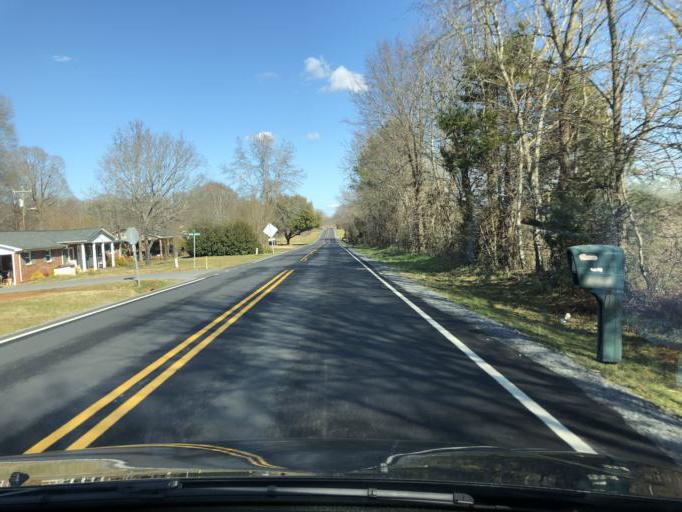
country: US
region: North Carolina
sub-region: Cleveland County
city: Shelby
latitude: 35.2066
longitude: -81.5467
